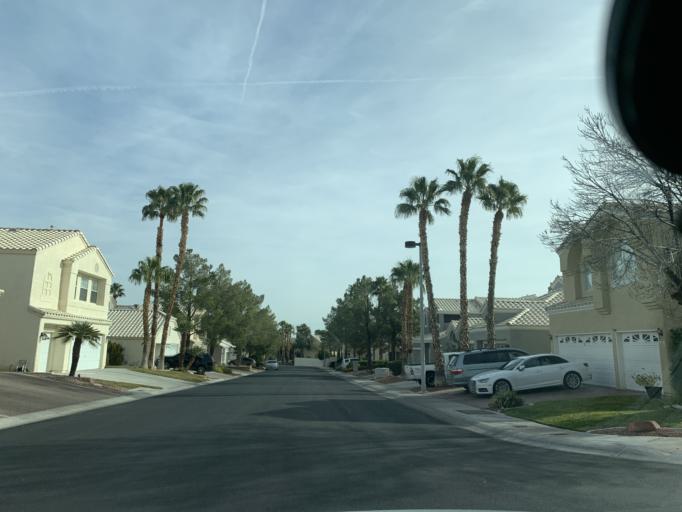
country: US
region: Nevada
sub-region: Clark County
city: Summerlin South
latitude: 36.1541
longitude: -115.2991
